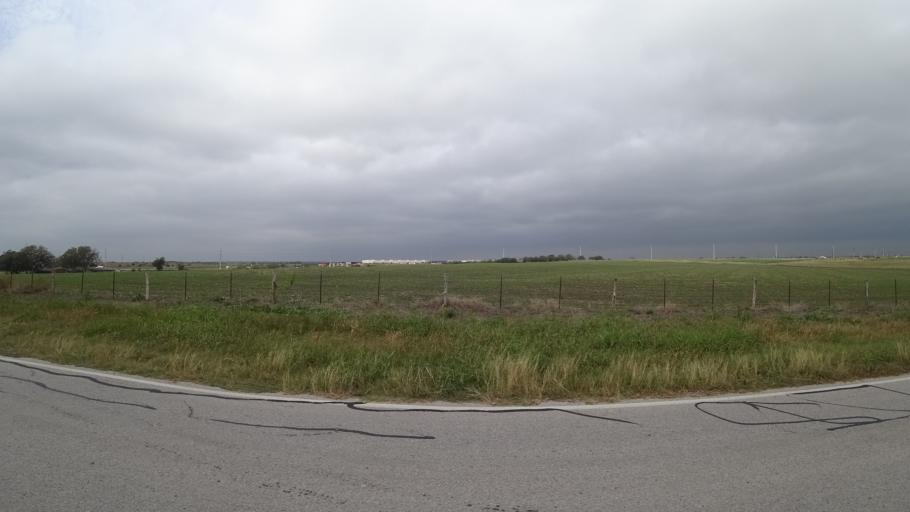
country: US
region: Texas
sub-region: Travis County
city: Pflugerville
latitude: 30.4134
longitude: -97.5784
